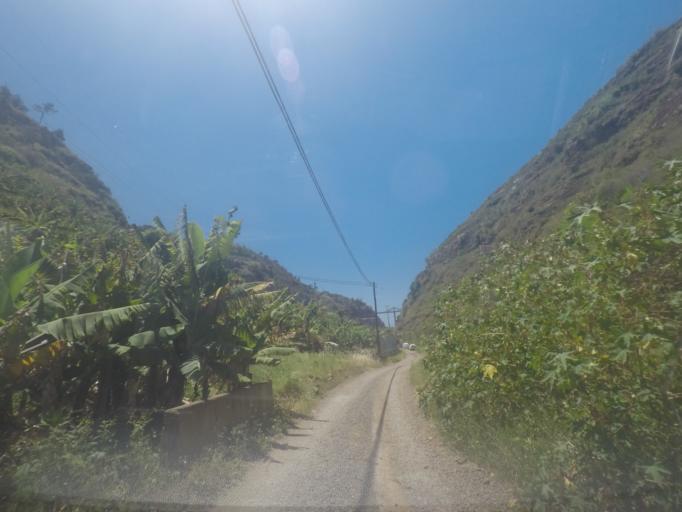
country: PT
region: Madeira
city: Camara de Lobos
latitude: 32.6652
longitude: -16.9601
